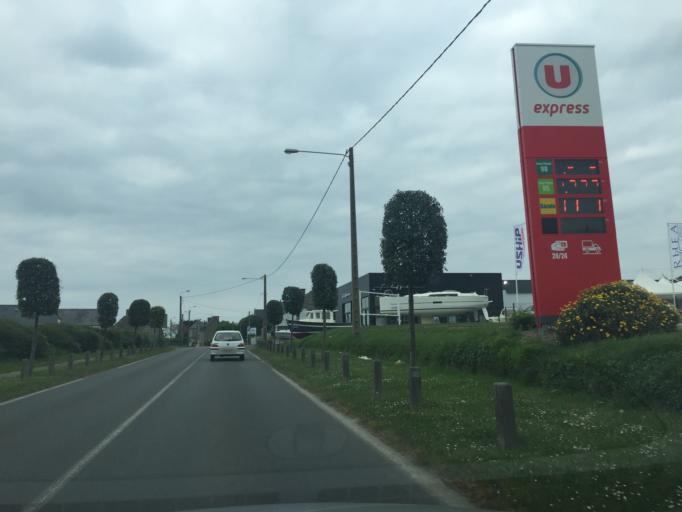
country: FR
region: Brittany
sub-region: Departement des Cotes-d'Armor
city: Saint-Cast-le-Guildo
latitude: 48.6181
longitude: -2.2662
